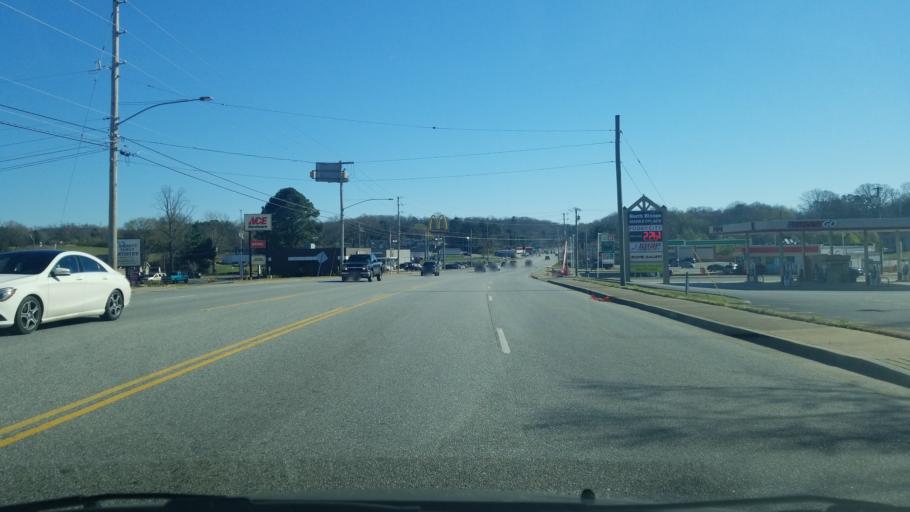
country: US
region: Tennessee
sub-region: Hamilton County
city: Middle Valley
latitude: 35.1998
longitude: -85.1605
